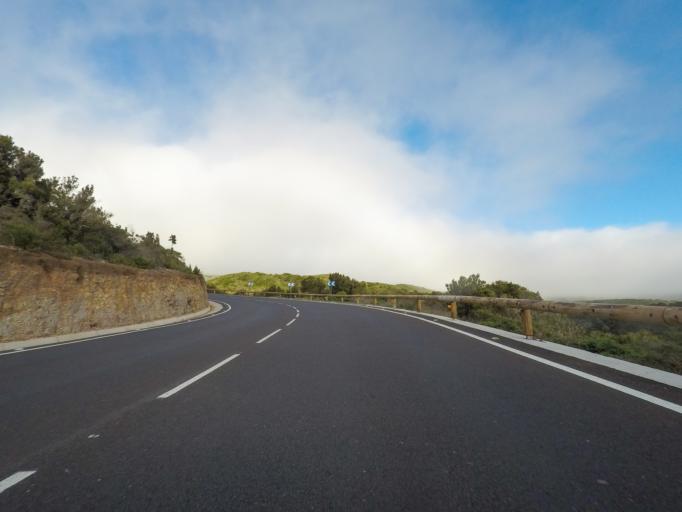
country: ES
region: Canary Islands
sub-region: Provincia de Santa Cruz de Tenerife
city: Vallehermosa
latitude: 28.1454
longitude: -17.3089
